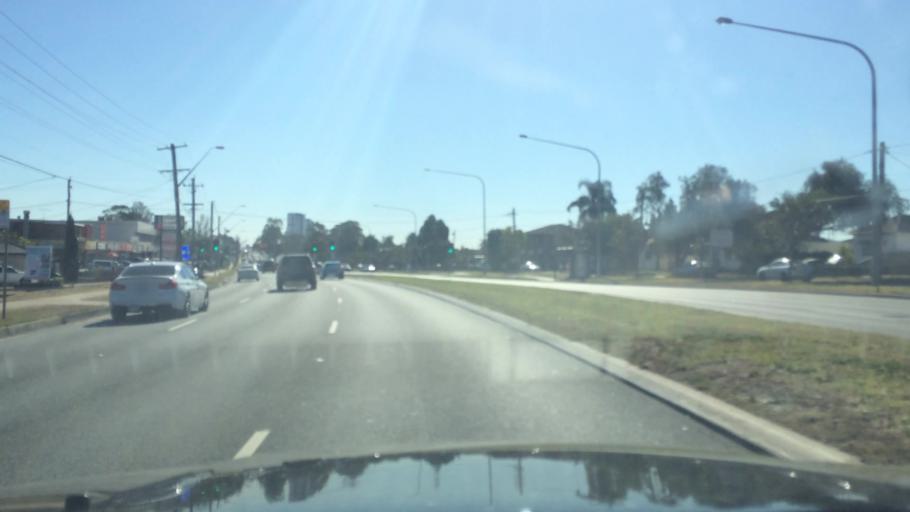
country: AU
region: New South Wales
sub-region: Campbelltown Municipality
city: Glenfield
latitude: -33.9444
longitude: 150.9107
